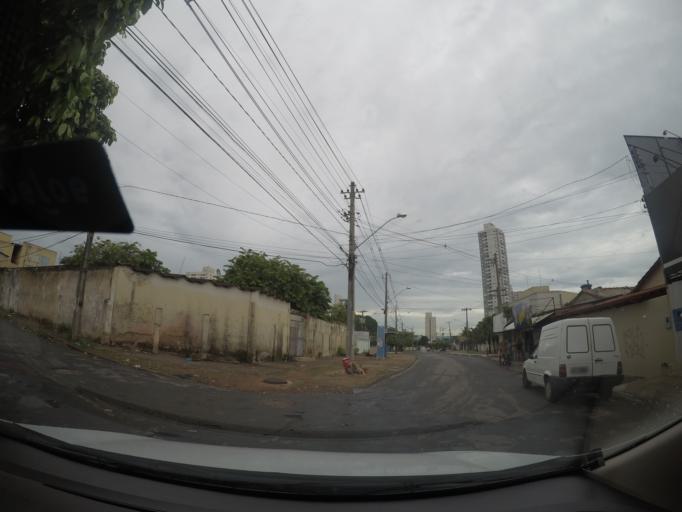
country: BR
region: Goias
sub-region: Goiania
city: Goiania
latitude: -16.6799
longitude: -49.2359
